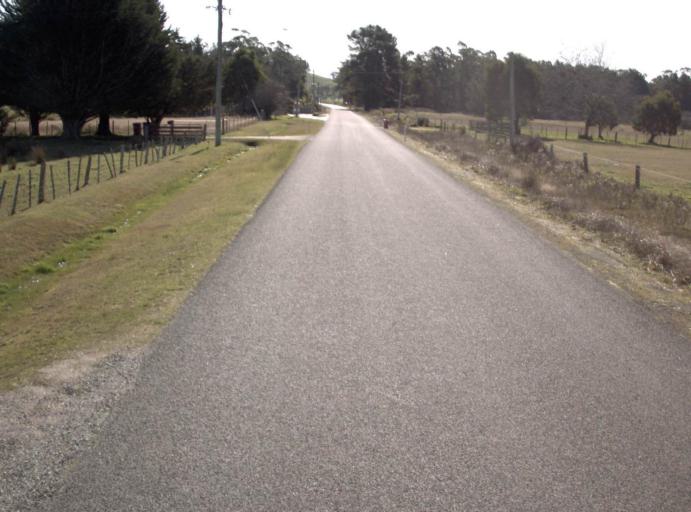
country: AU
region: Tasmania
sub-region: Launceston
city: Mayfield
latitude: -41.2587
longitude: 147.1545
